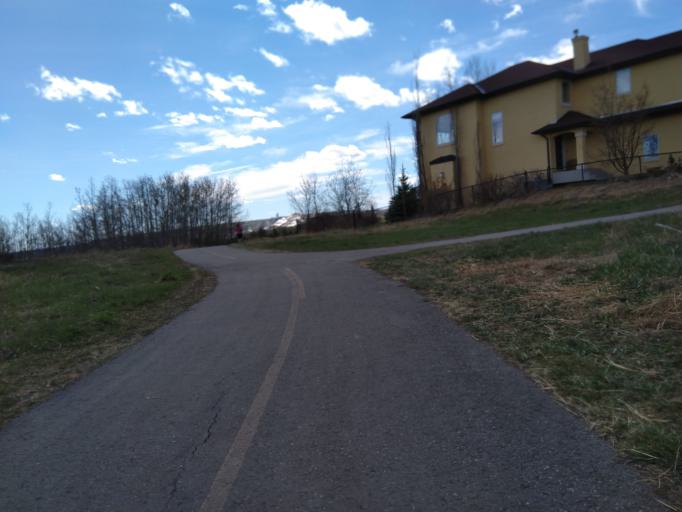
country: CA
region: Alberta
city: Calgary
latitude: 51.1180
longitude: -114.2371
